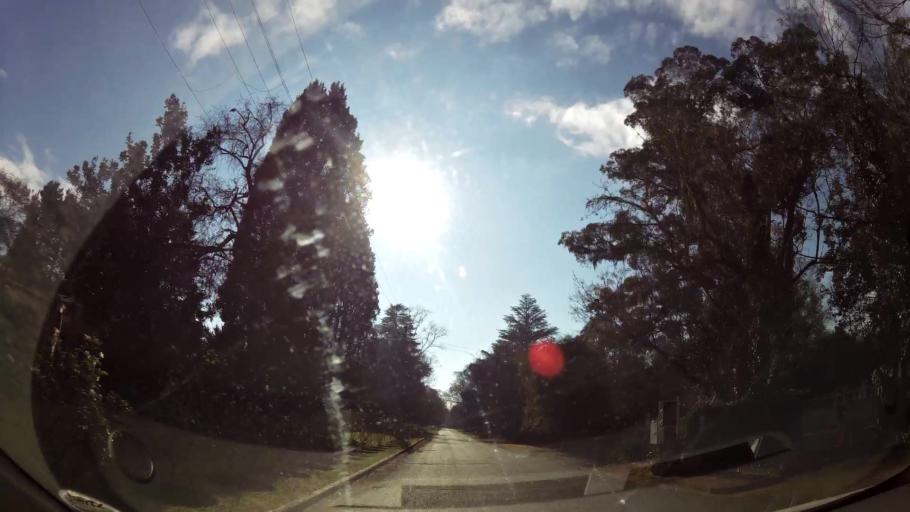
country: ZA
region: Gauteng
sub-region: Sedibeng District Municipality
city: Meyerton
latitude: -26.5474
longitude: 28.0628
